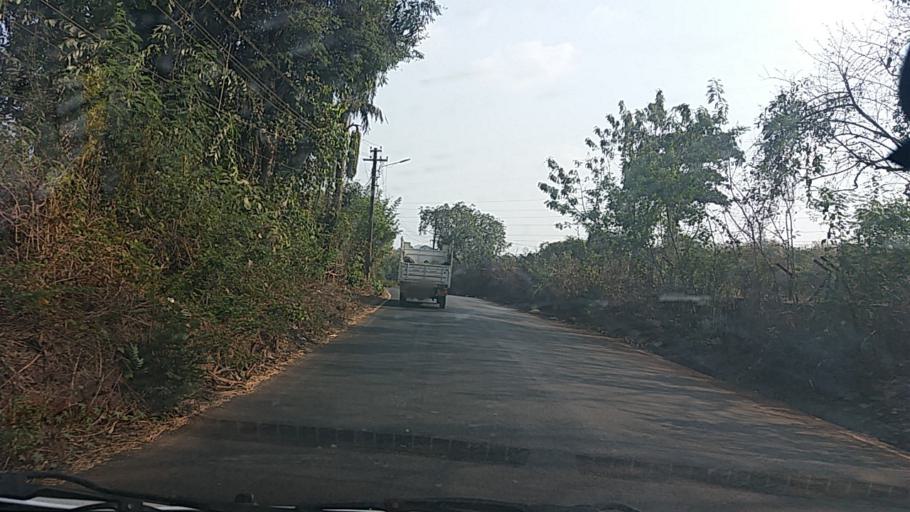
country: IN
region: Goa
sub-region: North Goa
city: Jua
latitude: 15.4867
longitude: 73.9230
